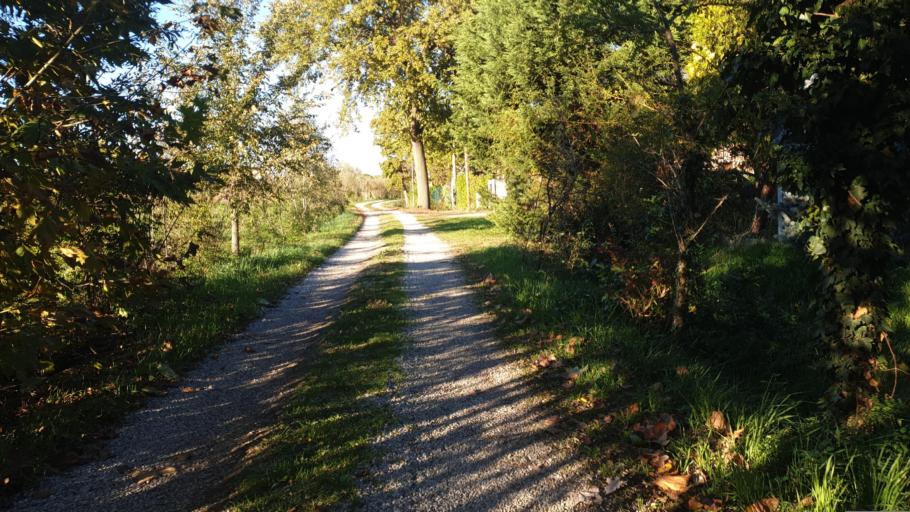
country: IT
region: Veneto
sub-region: Provincia di Venezia
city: Ballo
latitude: 45.4583
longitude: 12.0825
